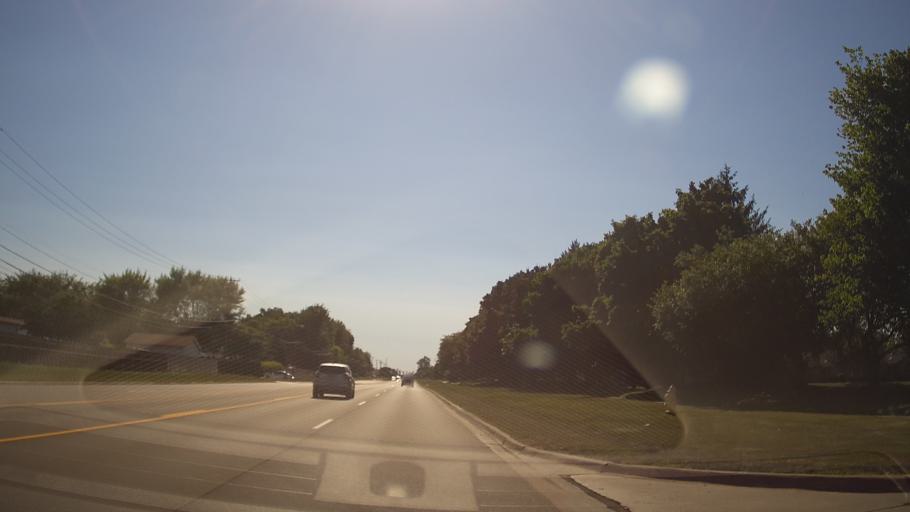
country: US
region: Michigan
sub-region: Macomb County
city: Clinton
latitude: 42.6132
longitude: -82.9443
